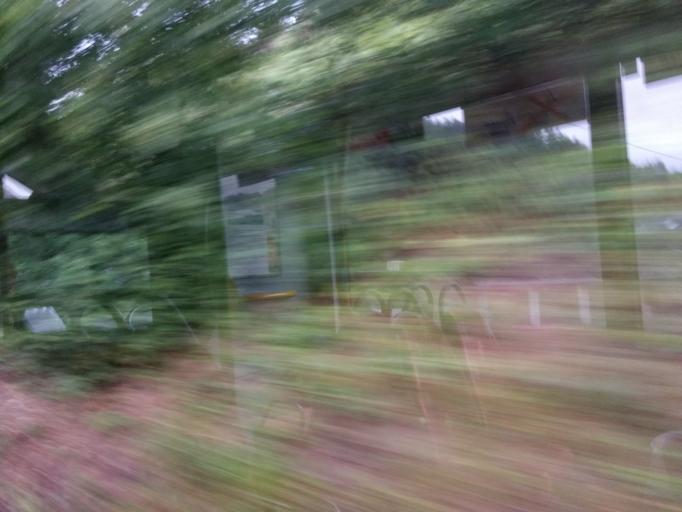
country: BE
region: Wallonia
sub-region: Province du Luxembourg
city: La Roche-en-Ardenne
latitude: 50.1682
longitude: 5.6256
